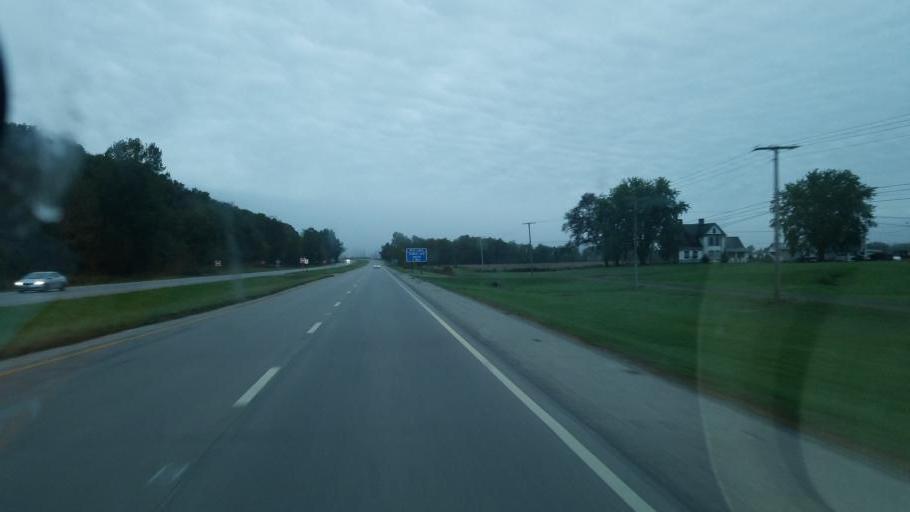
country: US
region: Ohio
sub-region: Scioto County
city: Lucasville
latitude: 38.9670
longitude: -83.0235
